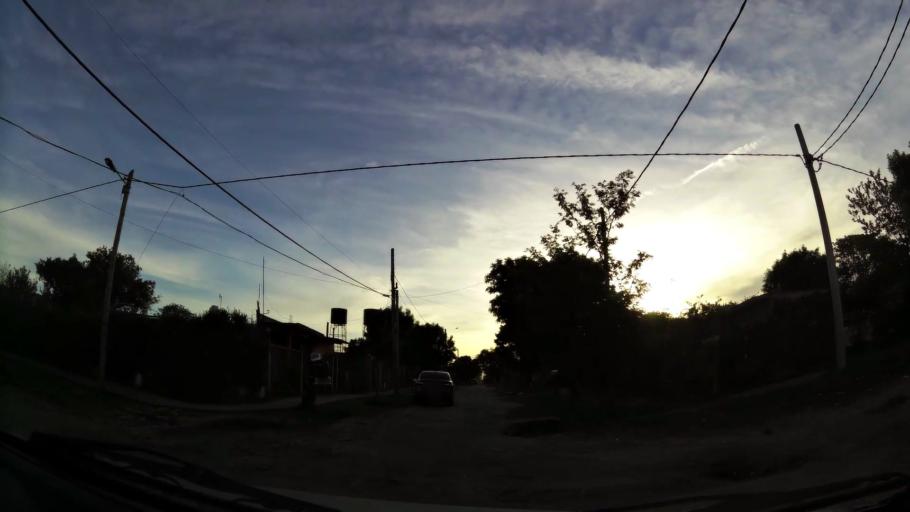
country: AR
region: Buenos Aires
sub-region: Partido de Almirante Brown
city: Adrogue
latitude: -34.7795
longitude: -58.3407
